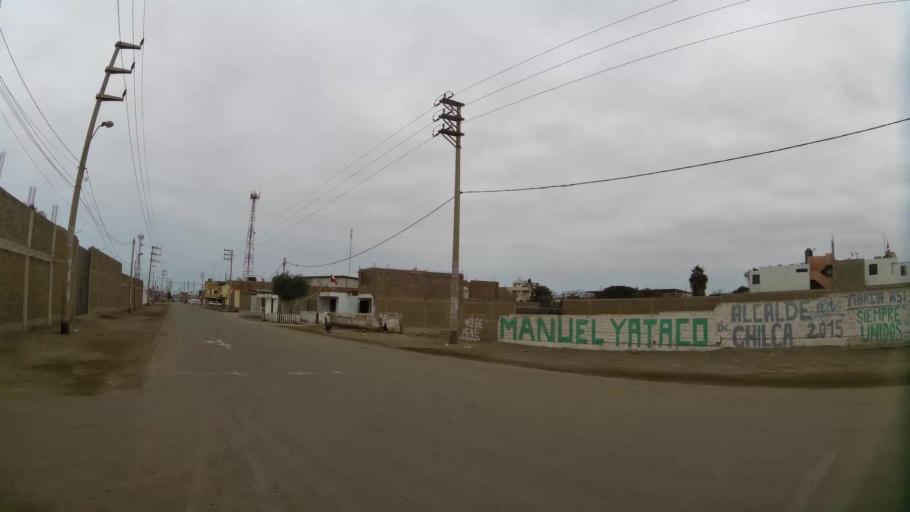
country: PE
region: Lima
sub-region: Provincia de Canete
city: Chilca
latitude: -12.5116
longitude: -76.7357
